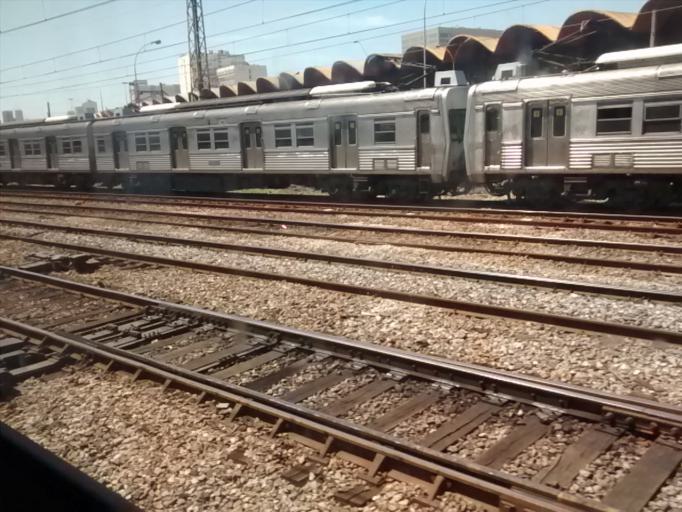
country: BR
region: Rio de Janeiro
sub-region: Rio De Janeiro
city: Rio de Janeiro
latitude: -22.9069
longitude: -43.2035
